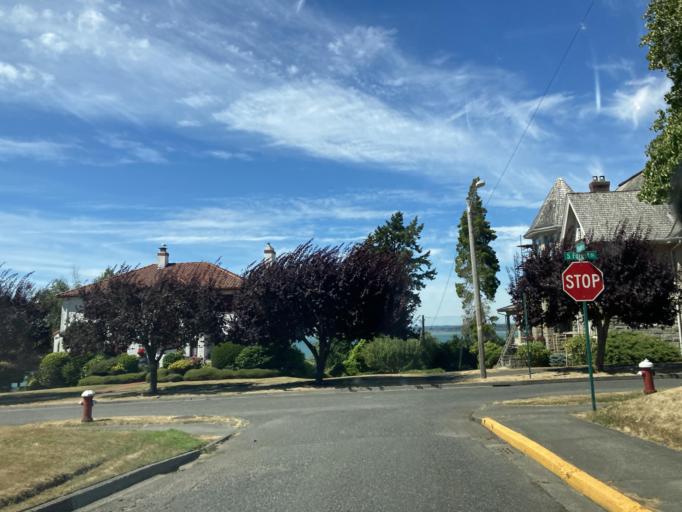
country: US
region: Washington
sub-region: Whatcom County
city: Bellingham
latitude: 48.7347
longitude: -122.4947
